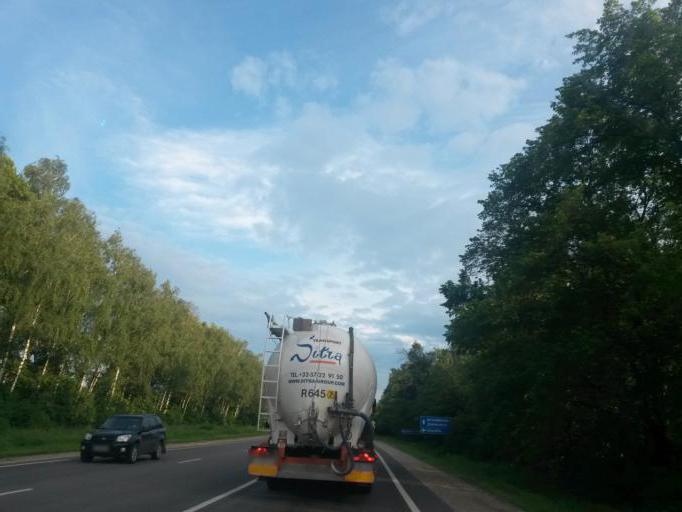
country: RU
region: Moskovskaya
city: Barybino
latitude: 55.2060
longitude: 37.8687
